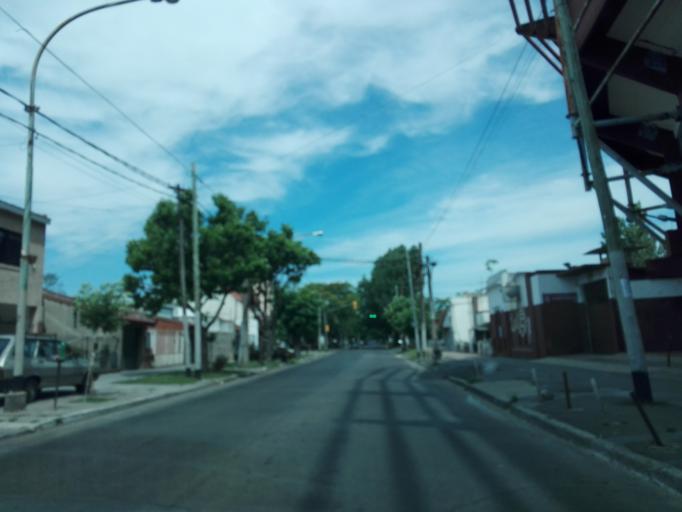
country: AR
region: Buenos Aires
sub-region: Partido de Lanus
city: Lanus
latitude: -34.7172
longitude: -58.3830
